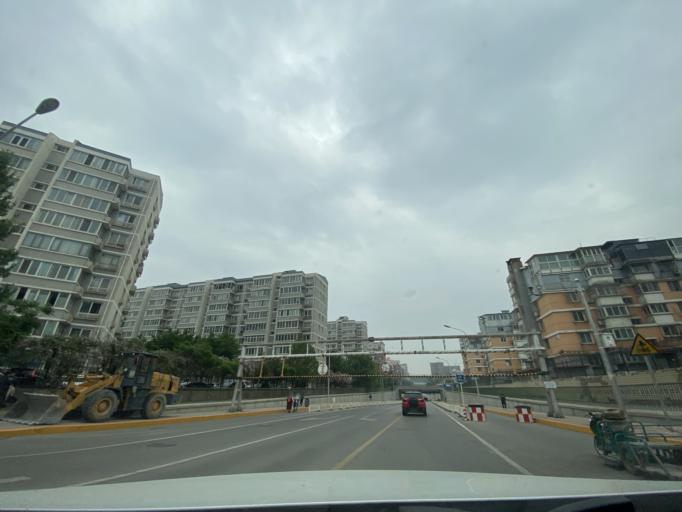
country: CN
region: Beijing
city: Sijiqing
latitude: 39.9327
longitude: 116.2420
